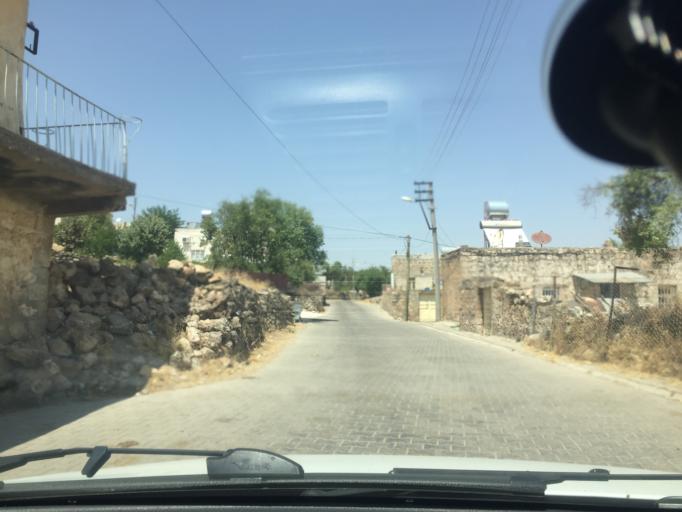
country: TR
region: Mardin
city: Kindirip
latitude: 37.4475
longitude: 41.2223
